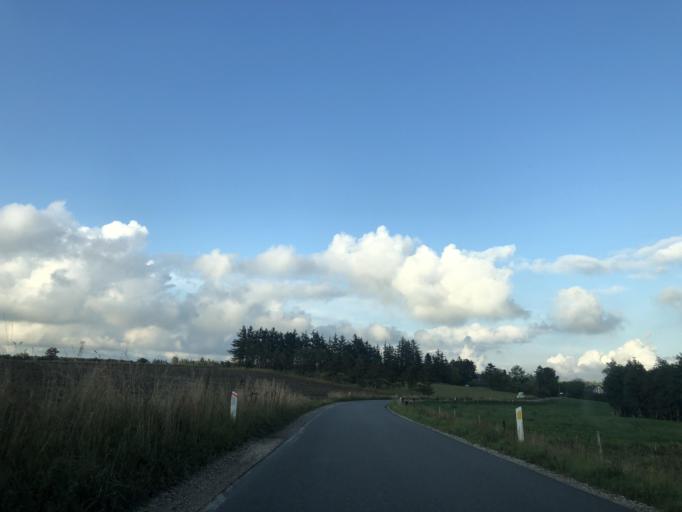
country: DK
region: North Denmark
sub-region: Alborg Kommune
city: Svenstrup
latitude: 56.9393
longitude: 9.7998
